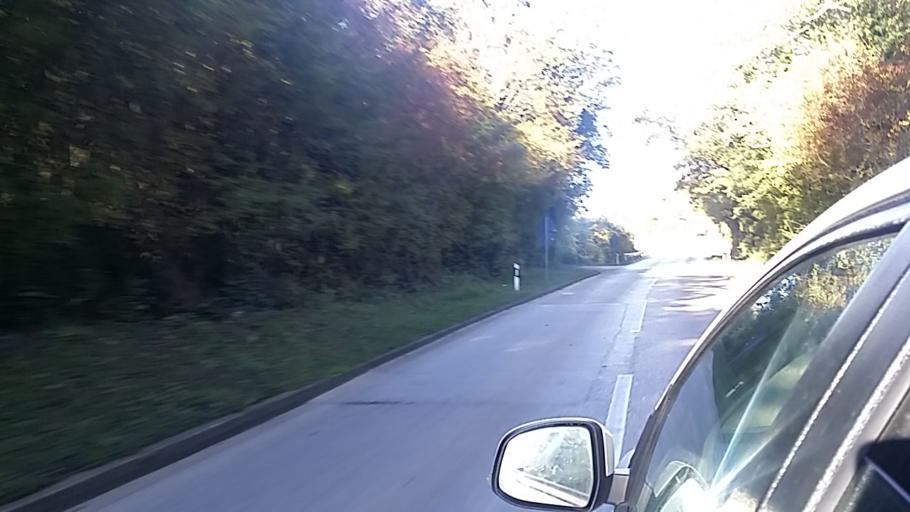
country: HR
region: Istarska
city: Vrsar
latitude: 45.1622
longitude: 13.6712
